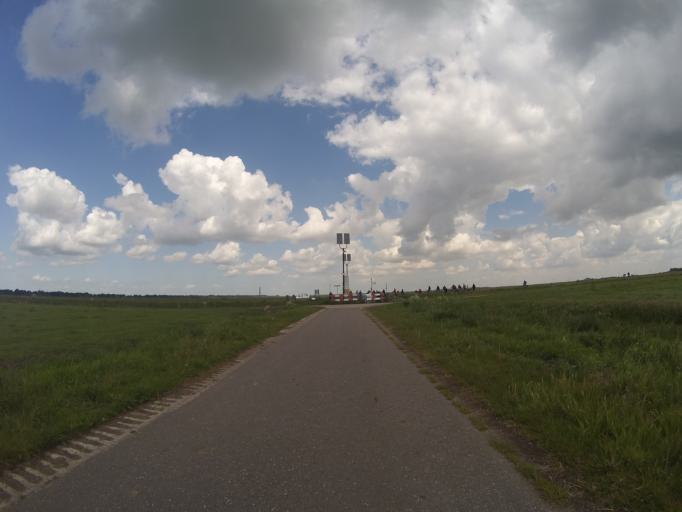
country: NL
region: Utrecht
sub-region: Gemeente Baarn
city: Baarn
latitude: 52.2483
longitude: 5.2872
